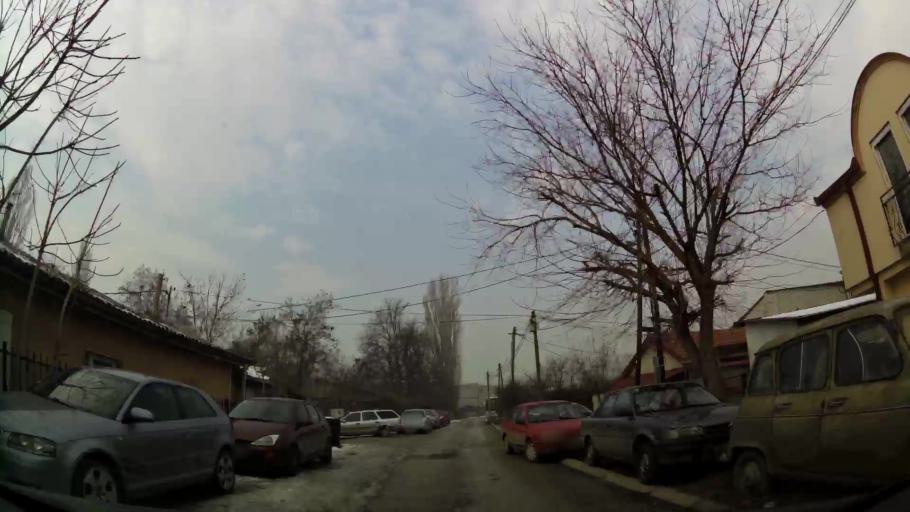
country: MK
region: Cair
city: Cair
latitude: 41.9951
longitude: 21.4590
